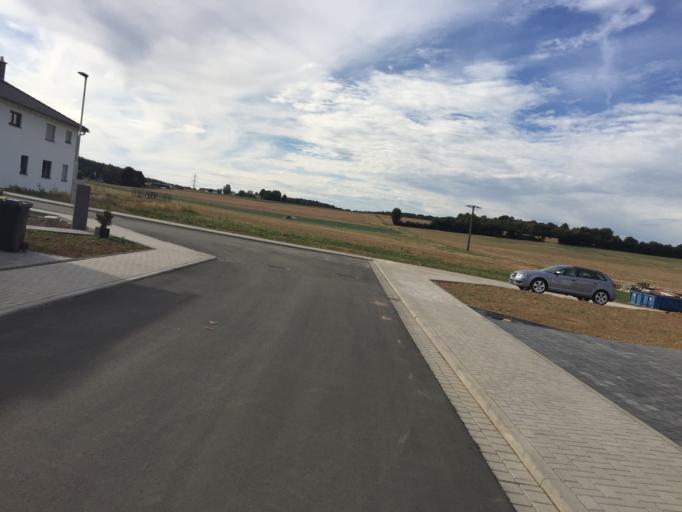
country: DE
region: Hesse
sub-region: Regierungsbezirk Giessen
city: Langgons
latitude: 50.4934
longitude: 8.7197
